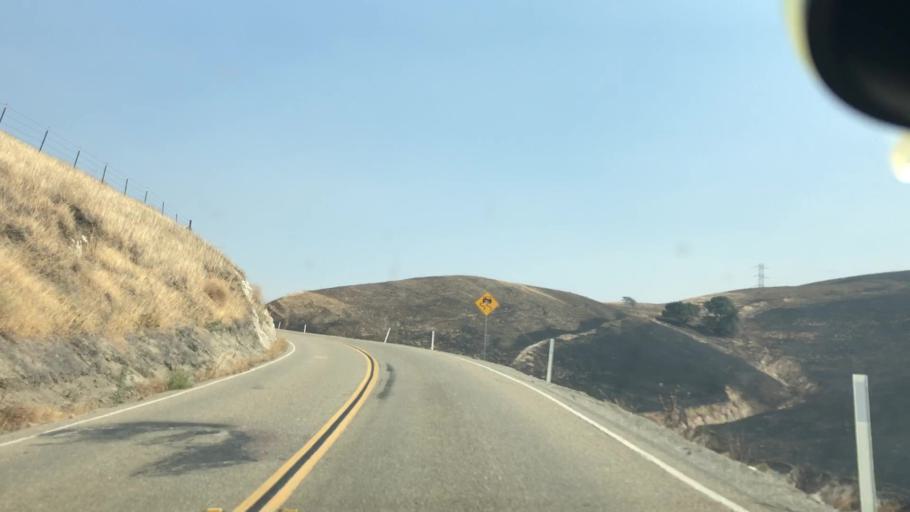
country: US
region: California
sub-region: San Joaquin County
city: Mountain House
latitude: 37.6502
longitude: -121.6125
